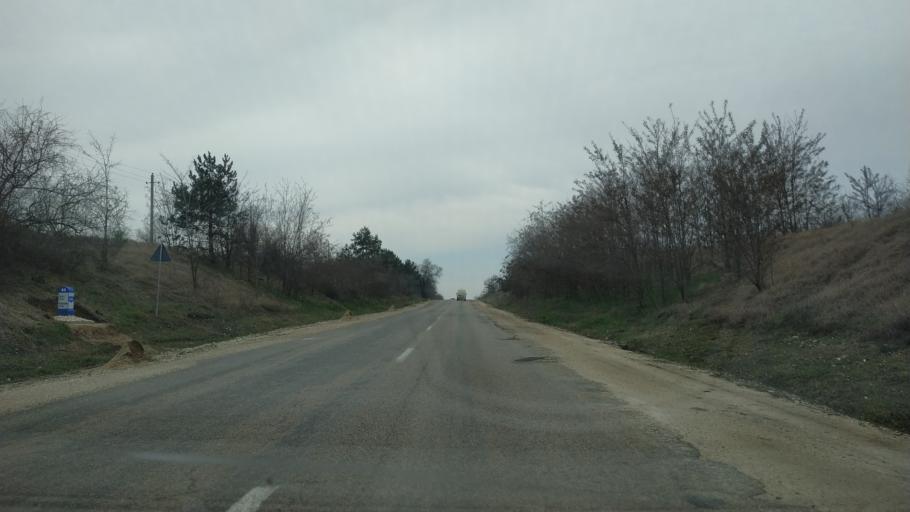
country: MD
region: Cahul
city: Cahul
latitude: 45.9583
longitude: 28.3741
